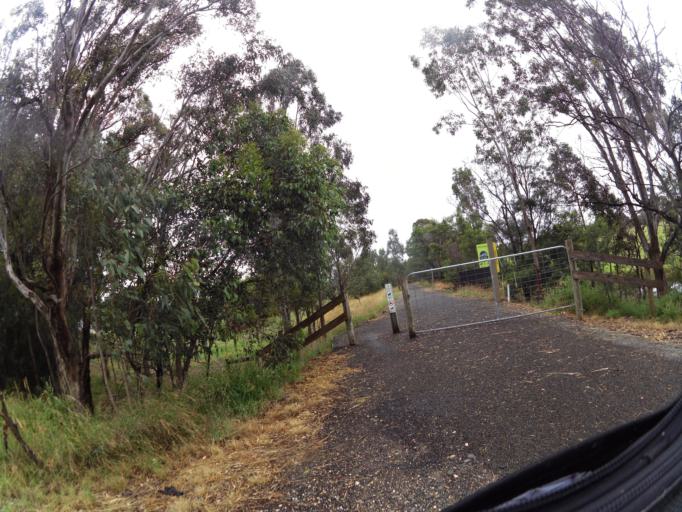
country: AU
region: Victoria
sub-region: East Gippsland
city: Bairnsdale
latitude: -37.8200
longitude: 147.7193
